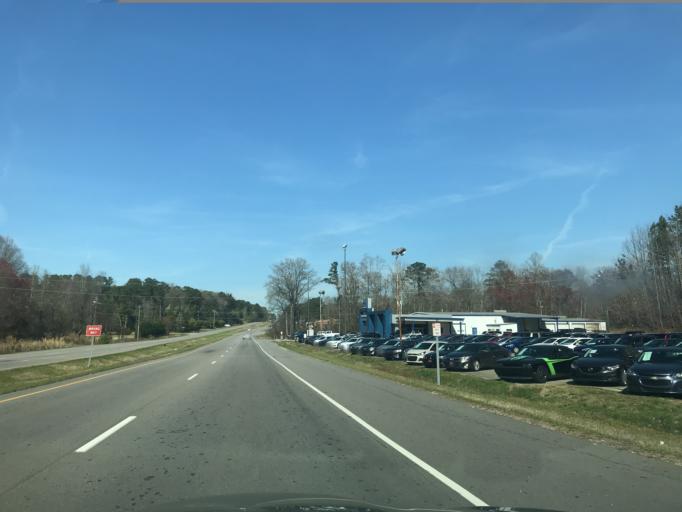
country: US
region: North Carolina
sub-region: Wake County
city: Fuquay-Varina
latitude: 35.6147
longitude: -78.7369
